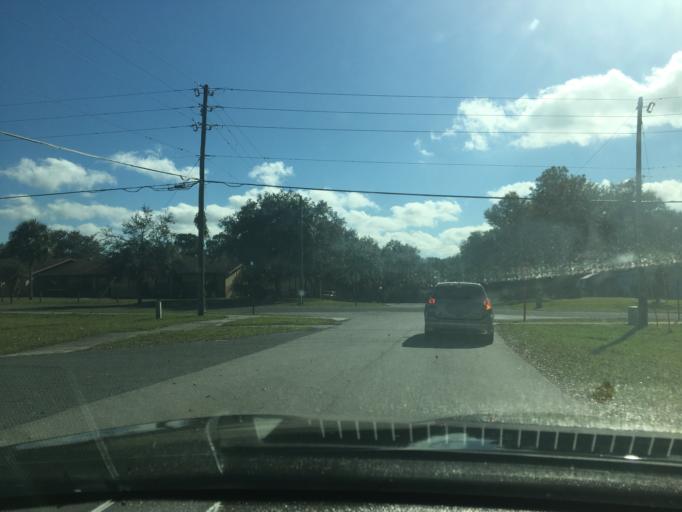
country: US
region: Florida
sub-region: Citrus County
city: Inverness
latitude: 28.8307
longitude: -82.3289
